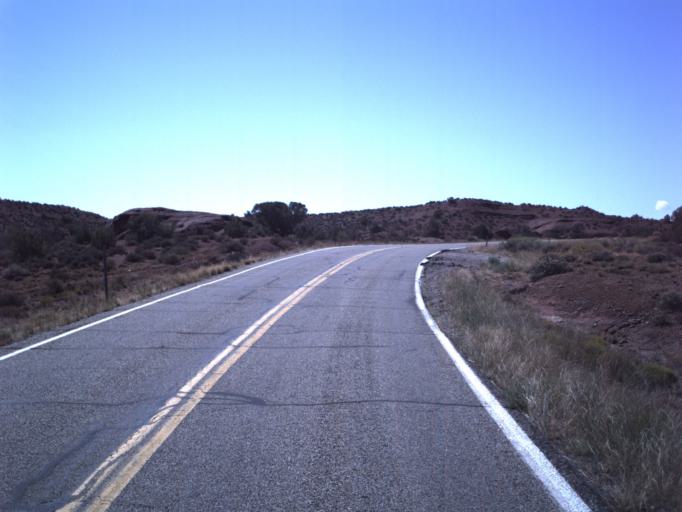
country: US
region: Utah
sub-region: Grand County
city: Moab
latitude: 38.7406
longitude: -109.3327
